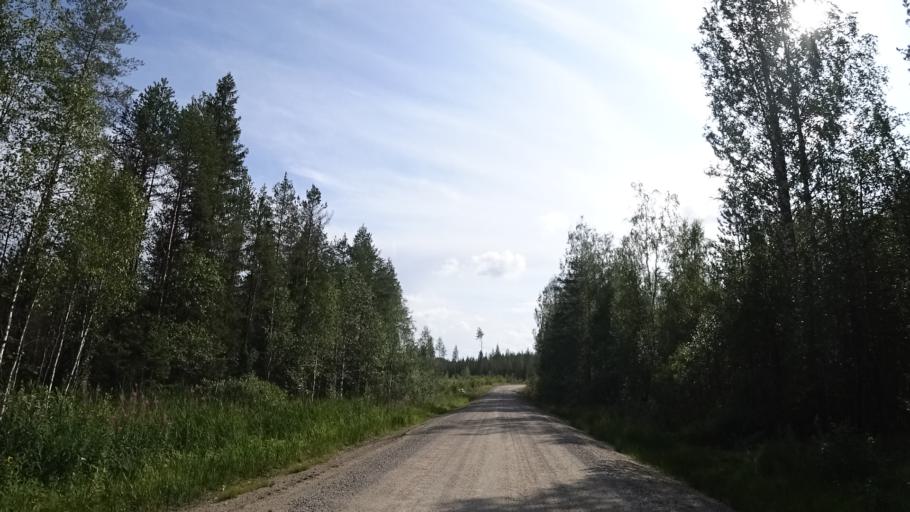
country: FI
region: North Karelia
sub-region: Pielisen Karjala
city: Lieksa
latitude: 63.5834
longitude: 30.1330
